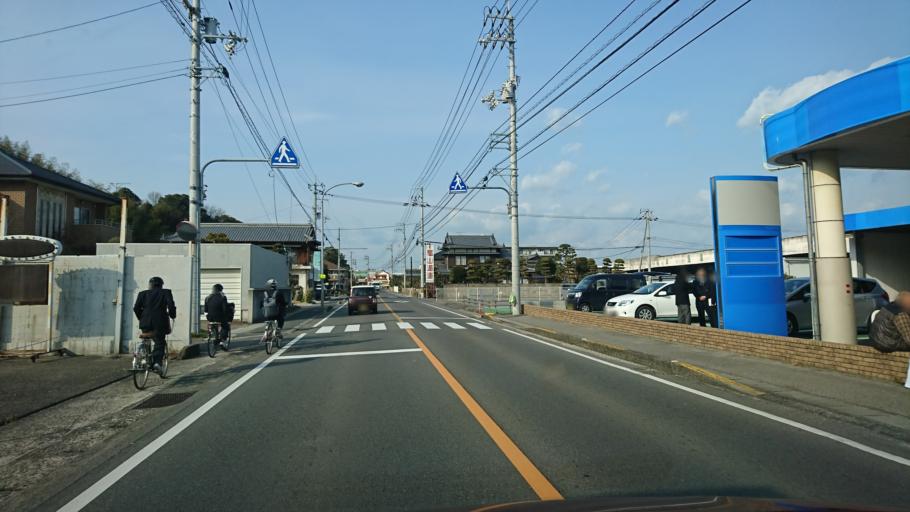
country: JP
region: Ehime
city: Saijo
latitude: 34.0326
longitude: 133.0355
